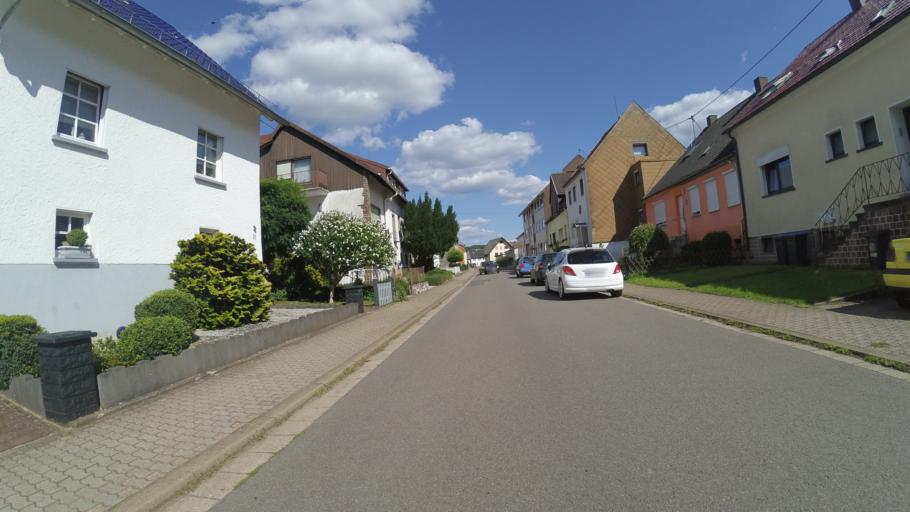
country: DE
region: Saarland
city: Illingen
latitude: 49.3887
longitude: 7.0656
